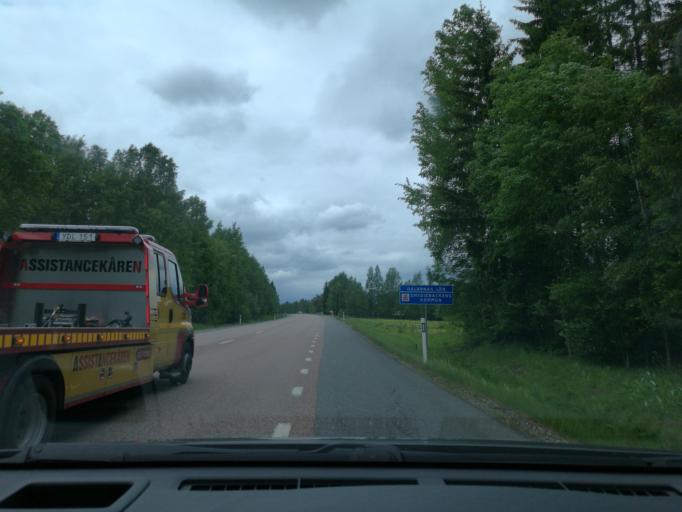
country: SE
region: Vaestmanland
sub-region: Fagersta Kommun
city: Fagersta
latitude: 59.9708
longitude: 15.7170
